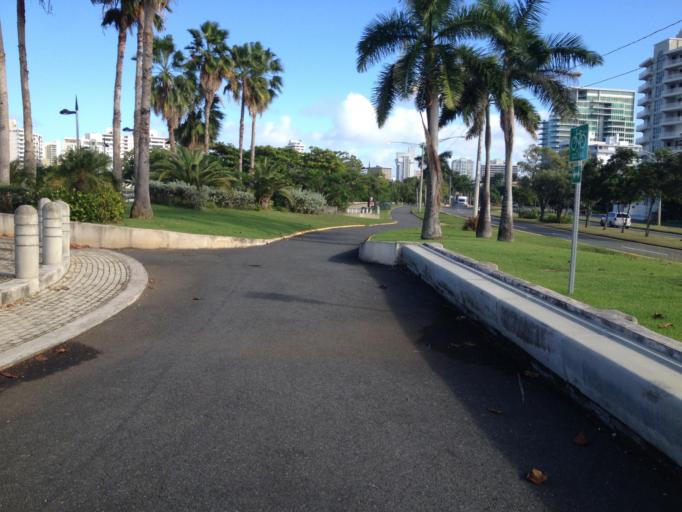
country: PR
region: San Juan
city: San Juan
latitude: 18.4568
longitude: -66.0801
